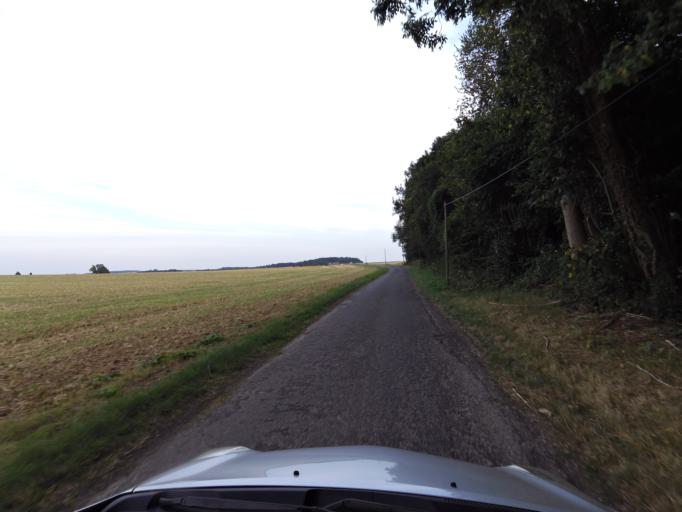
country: FR
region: Picardie
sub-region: Departement de l'Aisne
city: Bruyeres-et-Montberault
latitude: 49.5007
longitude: 3.6500
